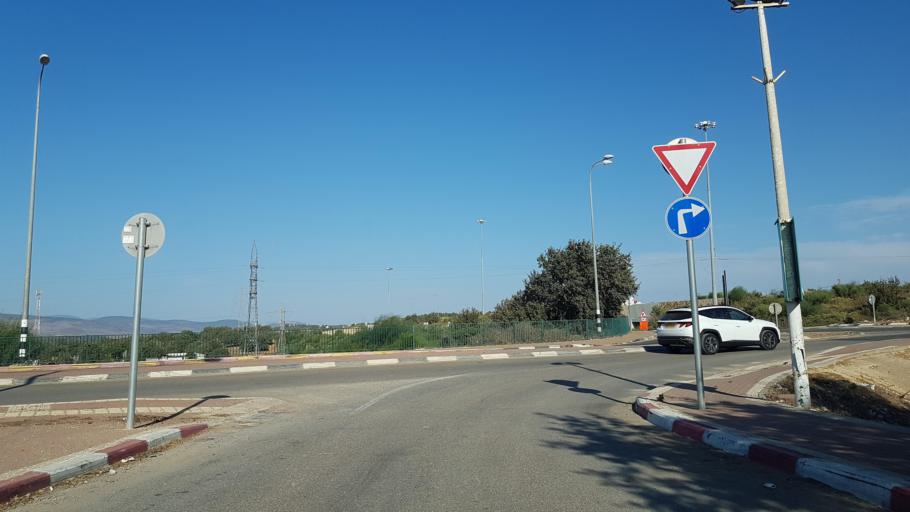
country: IL
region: Northern District
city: Timrat
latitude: 32.7343
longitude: 35.2097
